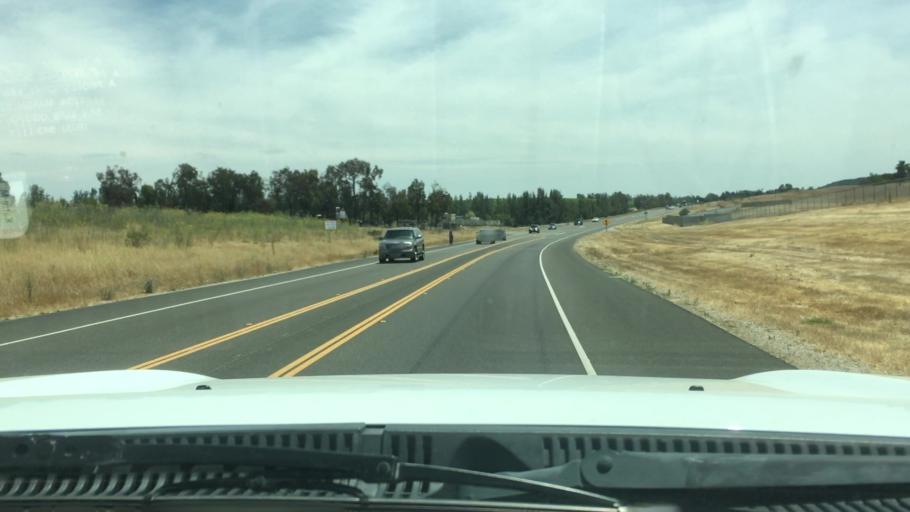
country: US
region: California
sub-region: San Luis Obispo County
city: San Luis Obispo
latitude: 35.2350
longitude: -120.6324
